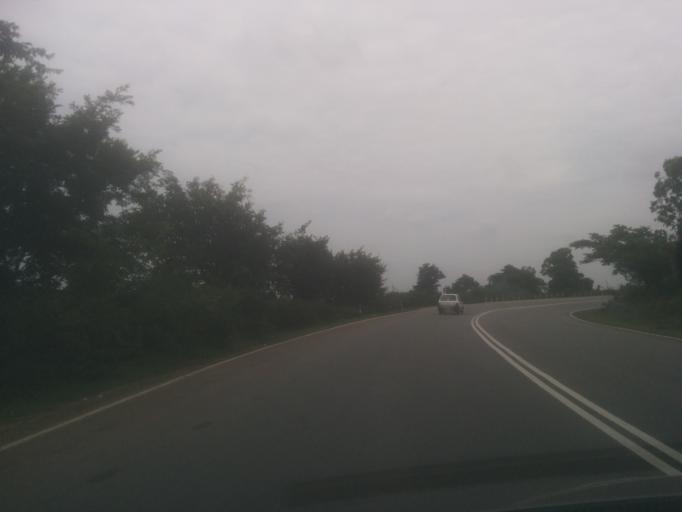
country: IN
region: Karnataka
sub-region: Hassan
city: Belur
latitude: 13.1634
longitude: 75.8985
